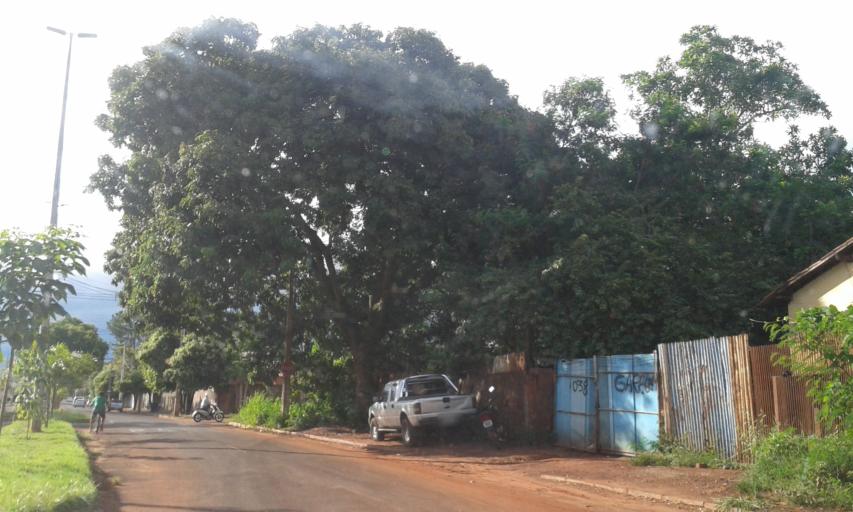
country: BR
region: Minas Gerais
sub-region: Ituiutaba
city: Ituiutaba
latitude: -18.9727
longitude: -49.4427
